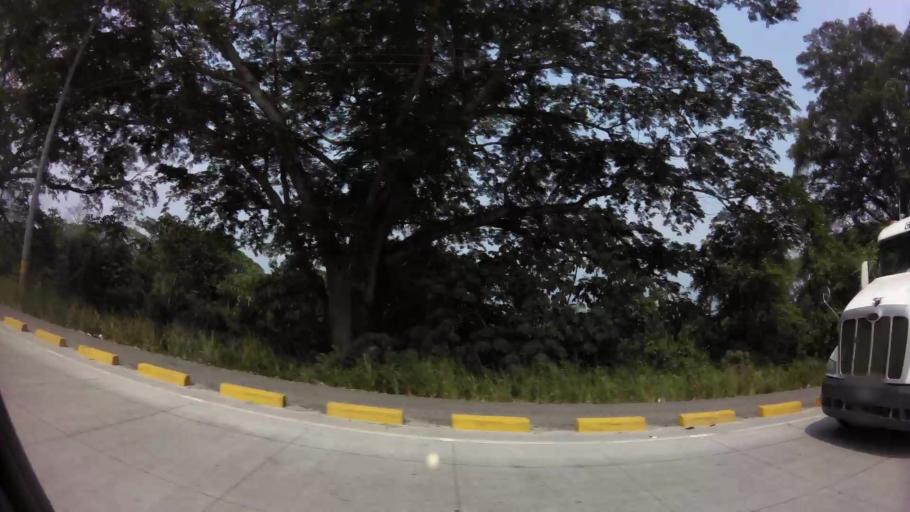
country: HN
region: Cortes
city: San Pedro Sula
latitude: 15.5274
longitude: -88.0050
